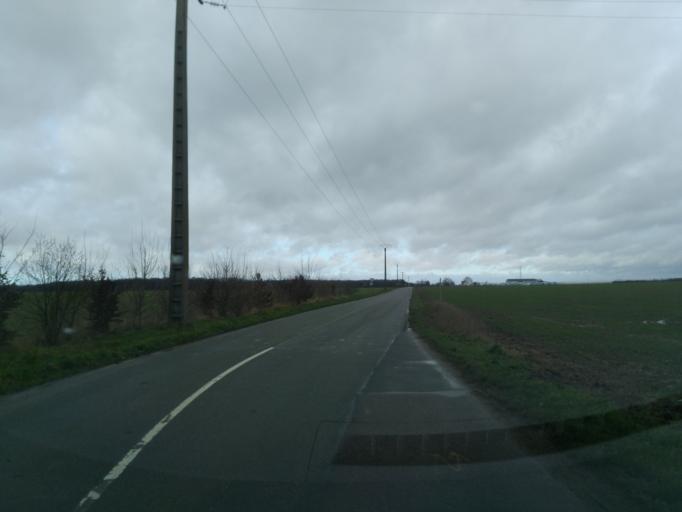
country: FR
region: Ile-de-France
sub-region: Departement des Yvelines
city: Feucherolles
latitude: 48.8930
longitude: 1.9617
